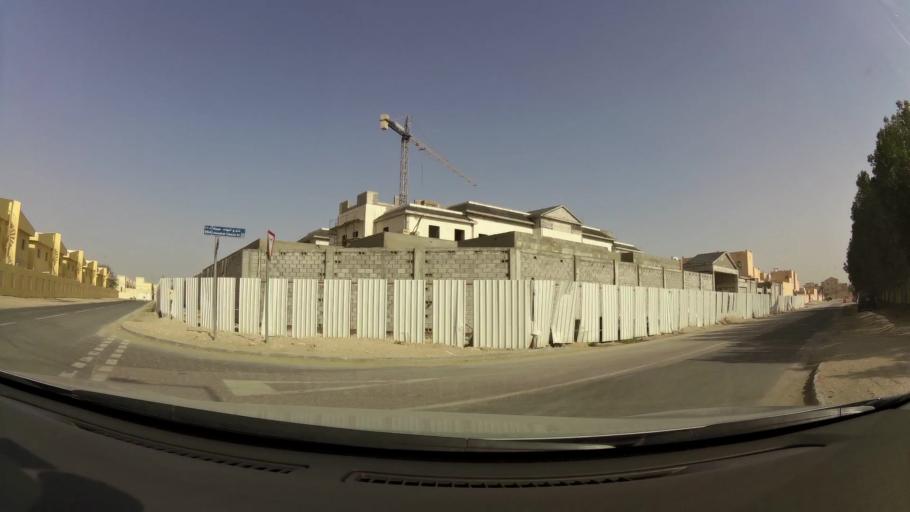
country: QA
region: Baladiyat ar Rayyan
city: Ar Rayyan
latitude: 25.3464
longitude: 51.4281
